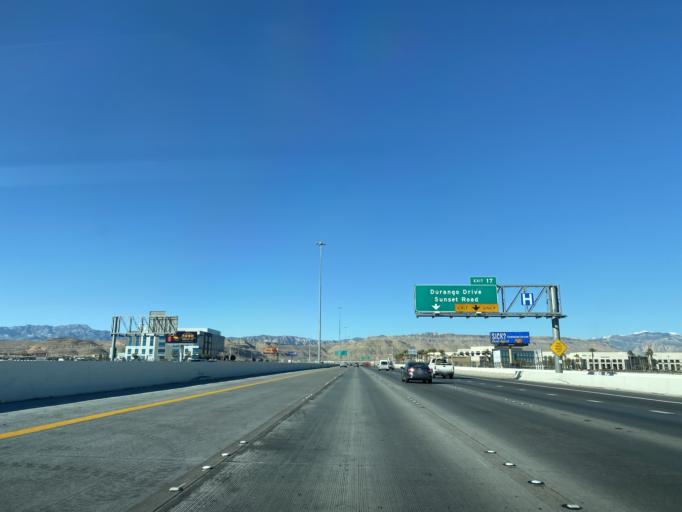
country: US
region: Nevada
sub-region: Clark County
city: Spring Valley
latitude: 36.0667
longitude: -115.2661
